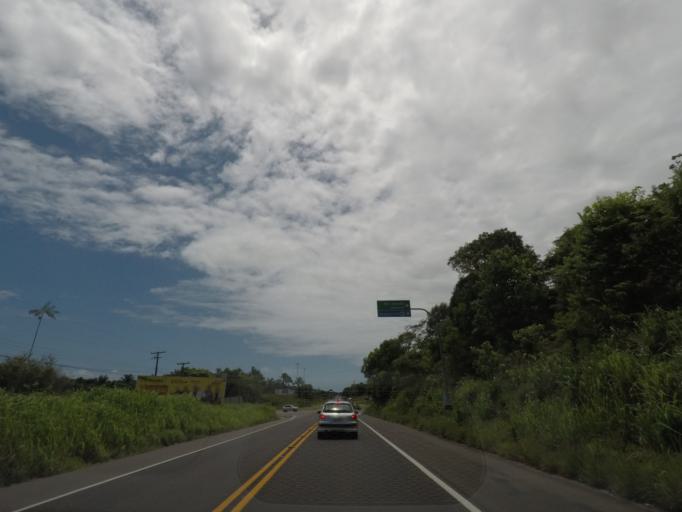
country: BR
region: Bahia
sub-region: Itaparica
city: Itaparica
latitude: -12.9488
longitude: -38.6321
